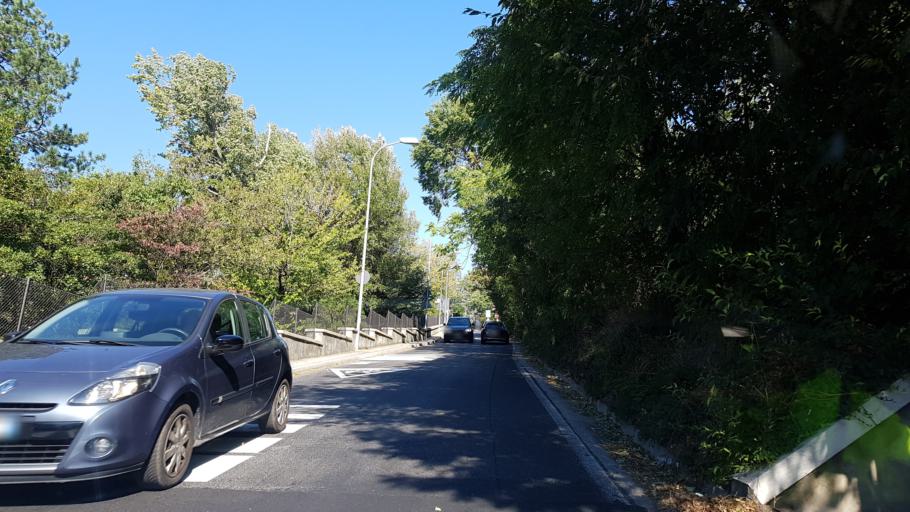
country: IT
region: Friuli Venezia Giulia
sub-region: Provincia di Trieste
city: Trieste
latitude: 45.6652
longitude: 13.7868
